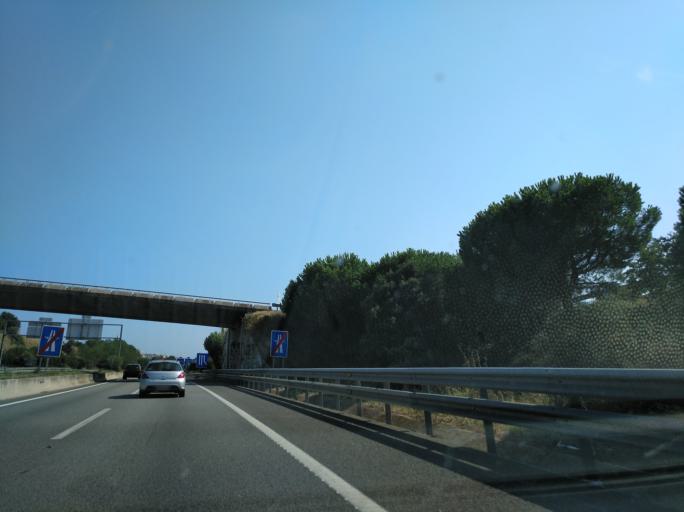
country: ES
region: Catalonia
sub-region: Provincia de Barcelona
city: Argentona
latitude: 41.5522
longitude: 2.4100
